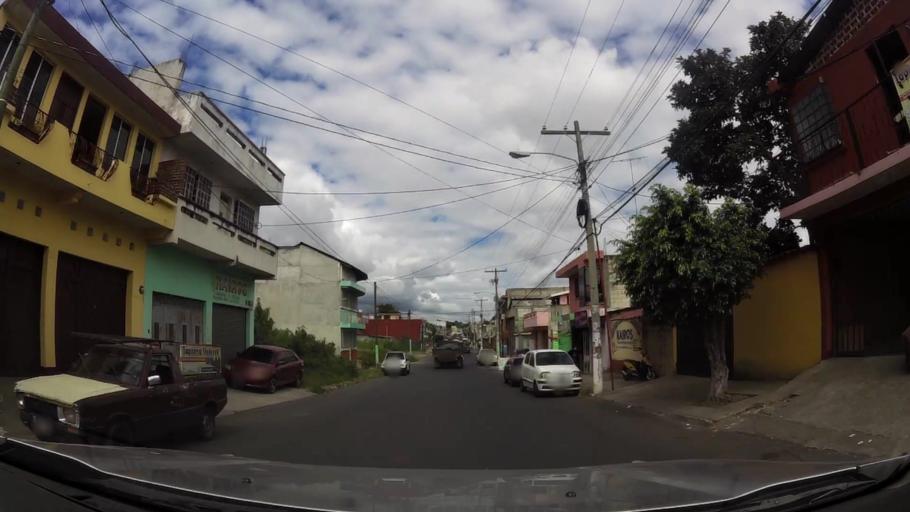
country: GT
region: Guatemala
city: Guatemala City
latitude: 14.6780
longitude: -90.5466
